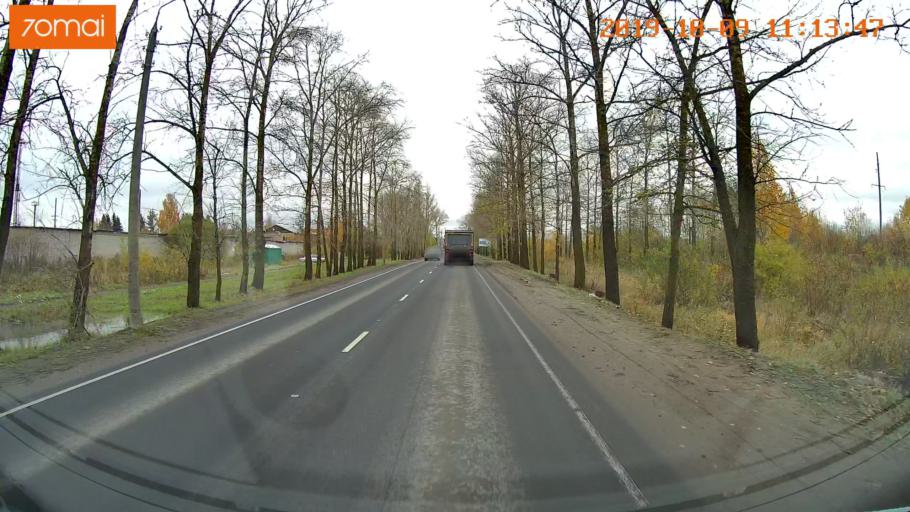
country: RU
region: Vologda
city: Vologda
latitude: 59.1842
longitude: 39.8469
